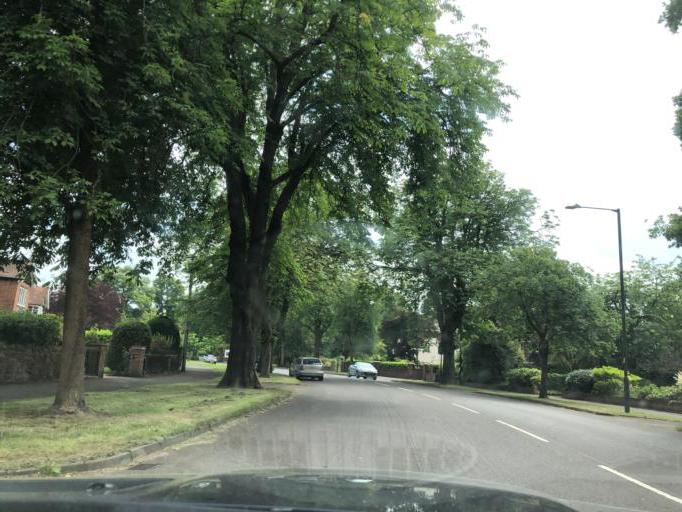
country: GB
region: England
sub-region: Warwickshire
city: Royal Leamington Spa
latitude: 52.2996
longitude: -1.5434
